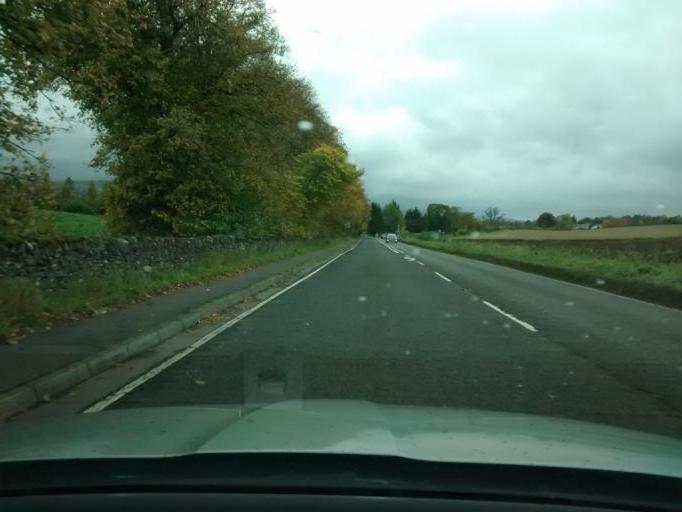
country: GB
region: Scotland
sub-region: Perth and Kinross
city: Auchterarder
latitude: 56.3069
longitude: -3.6749
